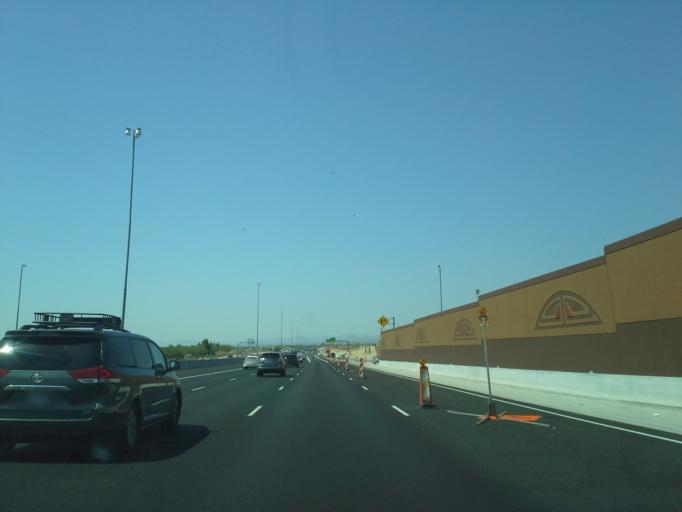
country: US
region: Arizona
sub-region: Maricopa County
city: Scottsdale
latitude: 33.5116
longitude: -111.8878
